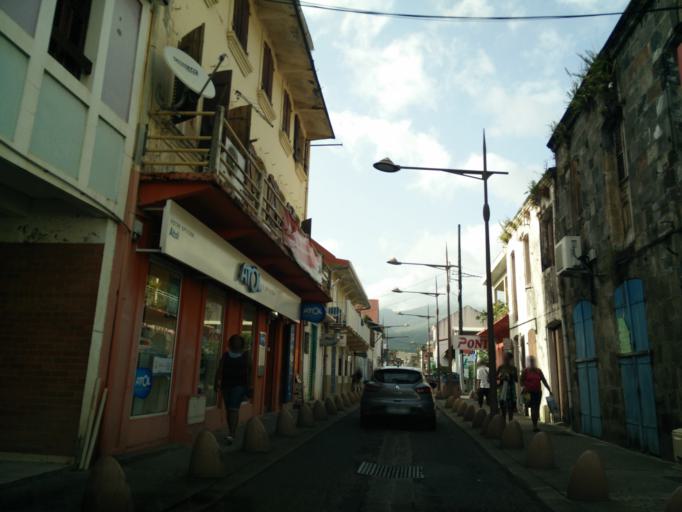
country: MQ
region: Martinique
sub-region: Martinique
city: Saint-Pierre
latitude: 14.7409
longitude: -61.1759
